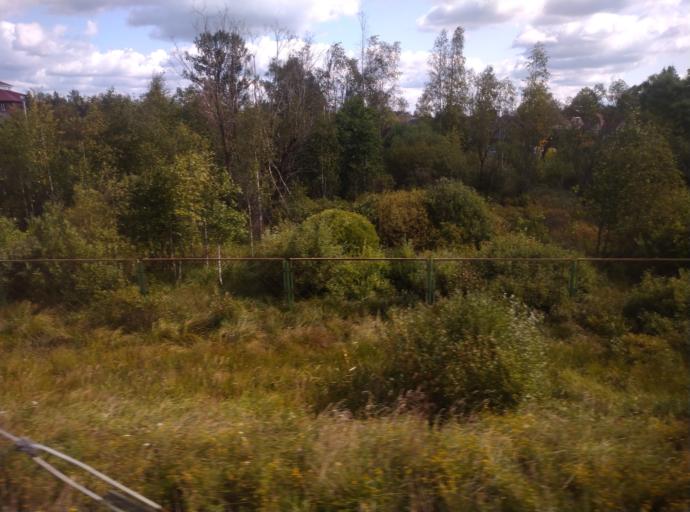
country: RU
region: Leningrad
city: Ul'yanovka
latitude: 59.6451
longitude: 30.7451
